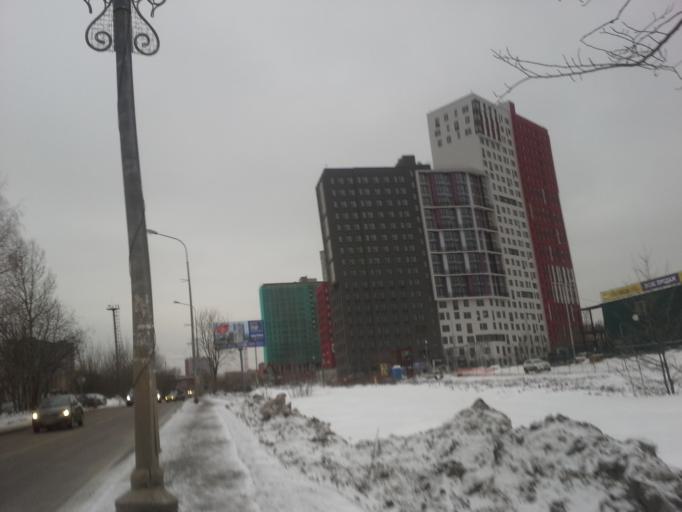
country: RU
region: Moskovskaya
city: Kommunarka
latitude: 55.5752
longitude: 37.4836
